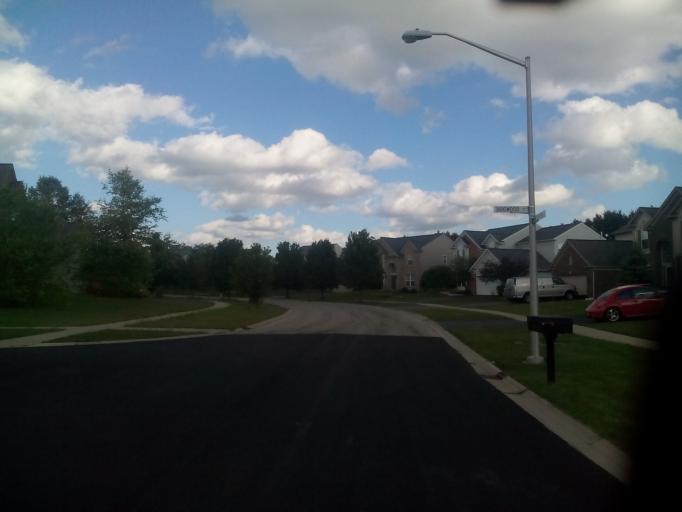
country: US
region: Illinois
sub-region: Will County
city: Bolingbrook
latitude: 41.6994
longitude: -88.1420
